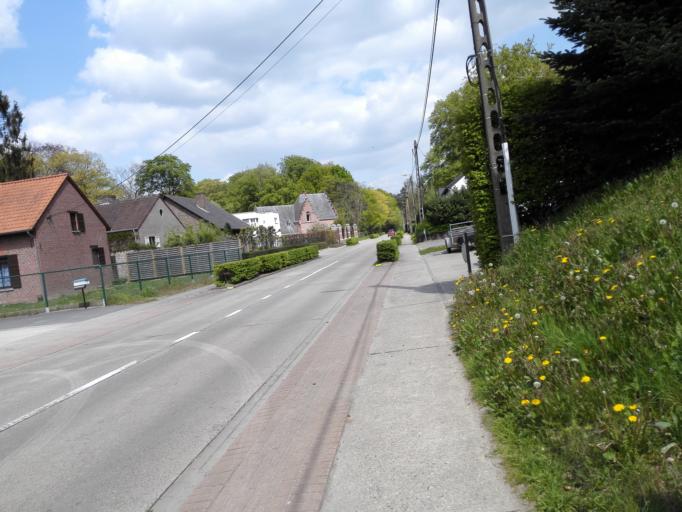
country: BE
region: Flanders
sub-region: Provincie Vlaams-Brabant
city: Rotselaar
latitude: 50.9666
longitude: 4.7405
